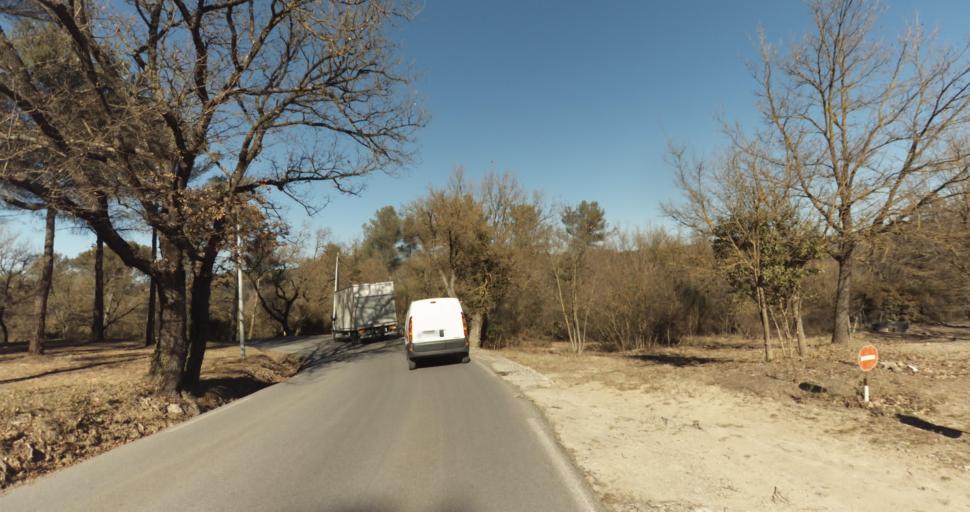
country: FR
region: Provence-Alpes-Cote d'Azur
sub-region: Departement des Bouches-du-Rhone
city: Peypin
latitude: 43.3931
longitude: 5.5708
